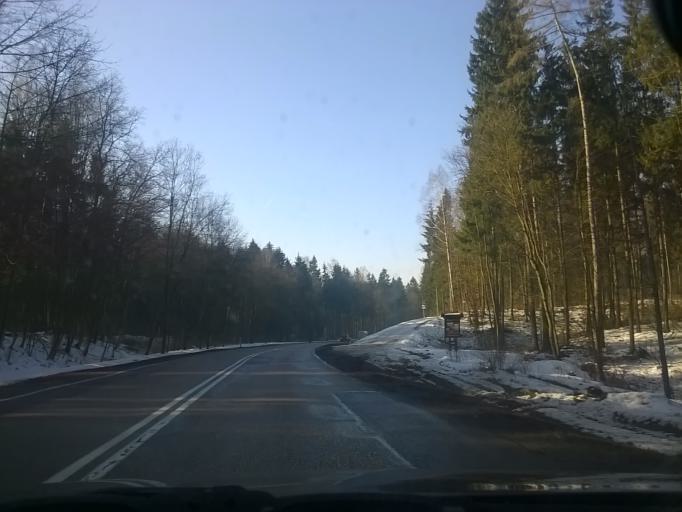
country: PL
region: Warmian-Masurian Voivodeship
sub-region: Powiat mragowski
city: Mragowo
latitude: 53.8370
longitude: 21.1947
